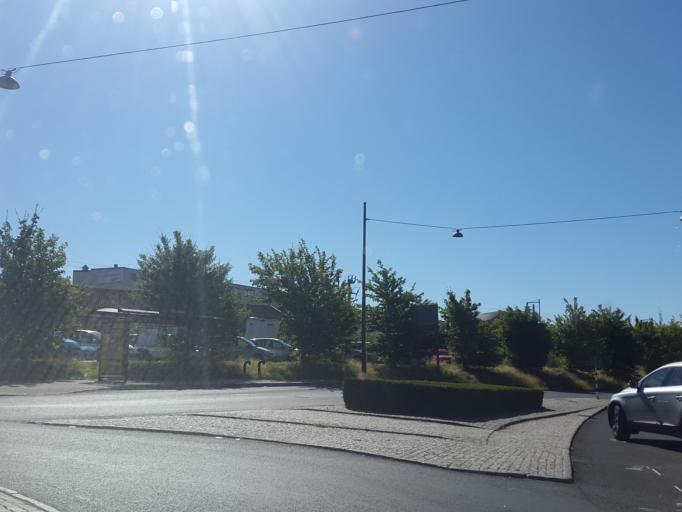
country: SE
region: Vaestra Goetaland
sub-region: Boras Kommun
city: Boras
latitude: 57.7300
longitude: 12.9404
